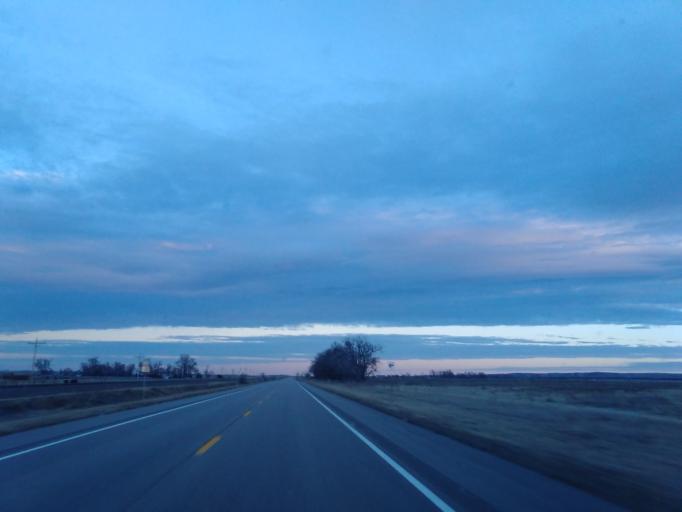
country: US
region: Nebraska
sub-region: Garden County
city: Oshkosh
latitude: 41.3942
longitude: -102.3097
